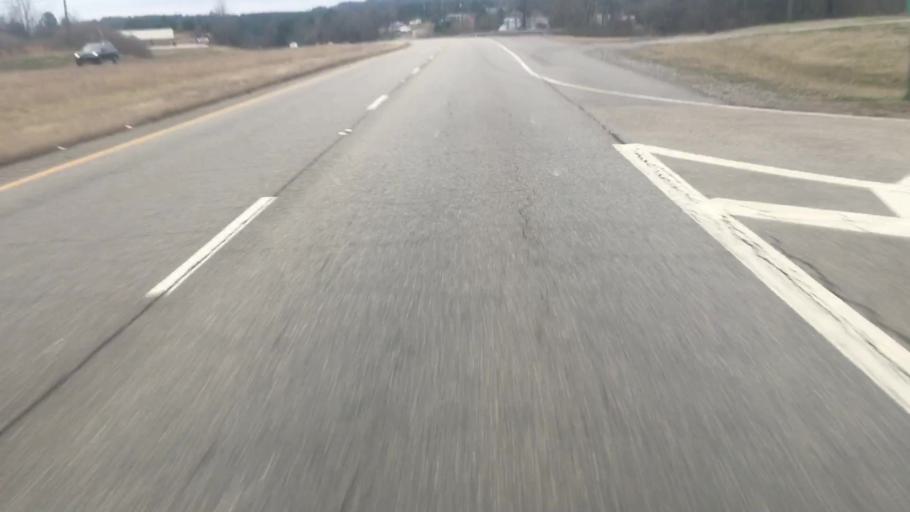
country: US
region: Alabama
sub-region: Walker County
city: Dora
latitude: 33.7966
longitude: -87.1107
